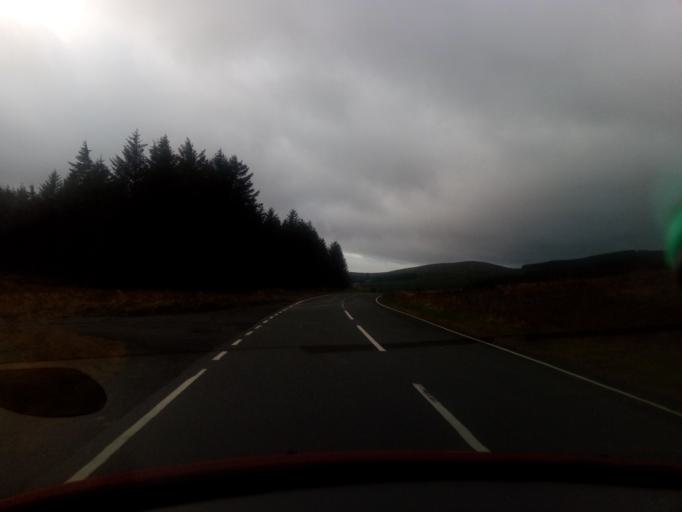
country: GB
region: Scotland
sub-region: The Scottish Borders
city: Hawick
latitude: 55.3187
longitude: -2.6497
